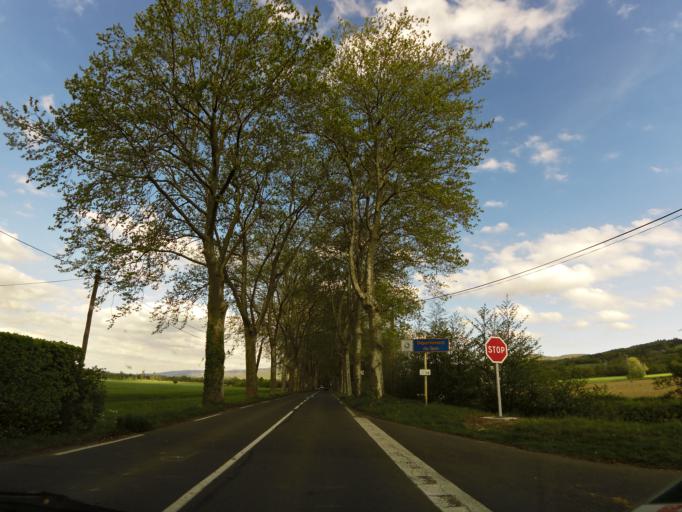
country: FR
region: Midi-Pyrenees
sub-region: Departement de la Haute-Garonne
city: Revel
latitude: 43.4536
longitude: 2.0198
